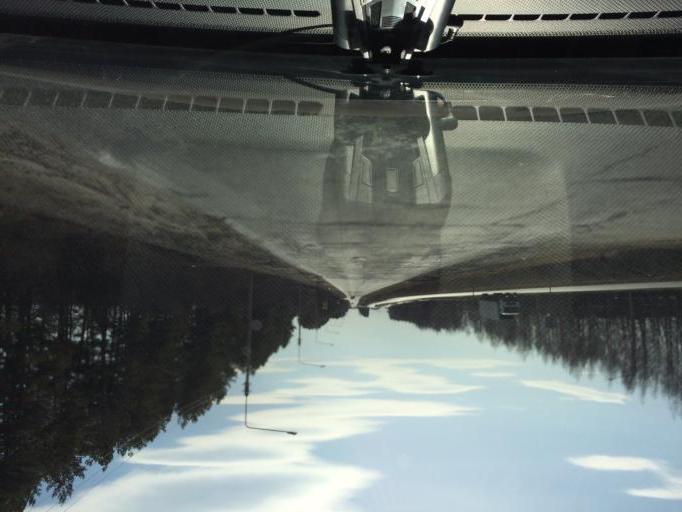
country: RU
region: Mariy-El
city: Yoshkar-Ola
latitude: 56.7238
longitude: 48.1177
